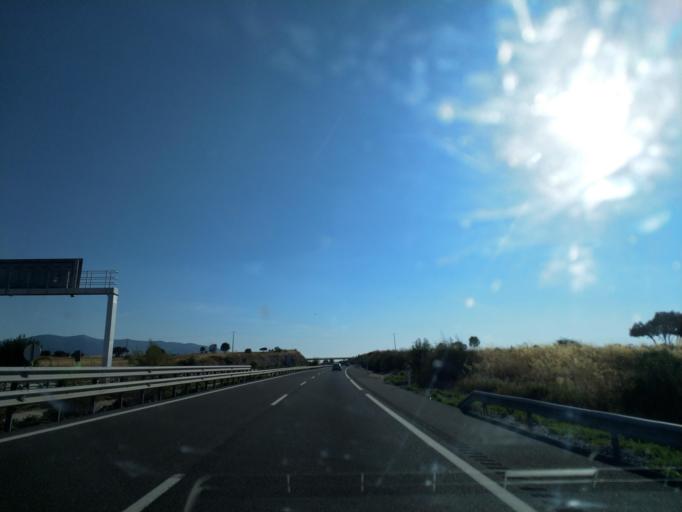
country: ES
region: Castille and Leon
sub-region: Provincia de Segovia
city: Segovia
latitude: 40.8976
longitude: -4.1081
